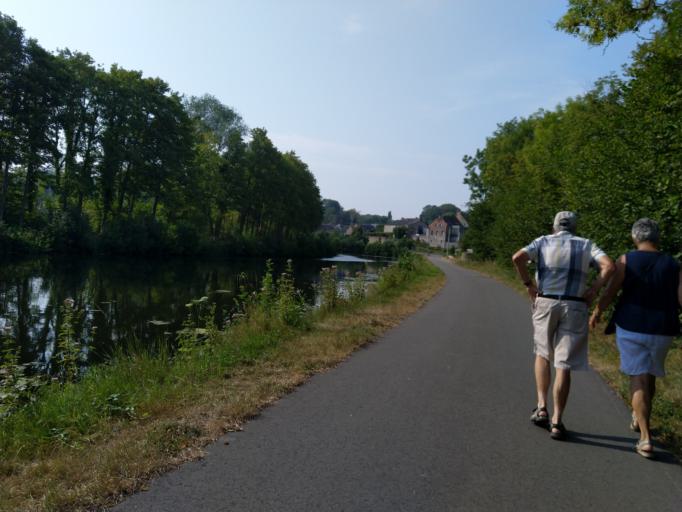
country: BE
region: Wallonia
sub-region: Province du Hainaut
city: Seneffe
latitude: 50.5690
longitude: 4.2569
